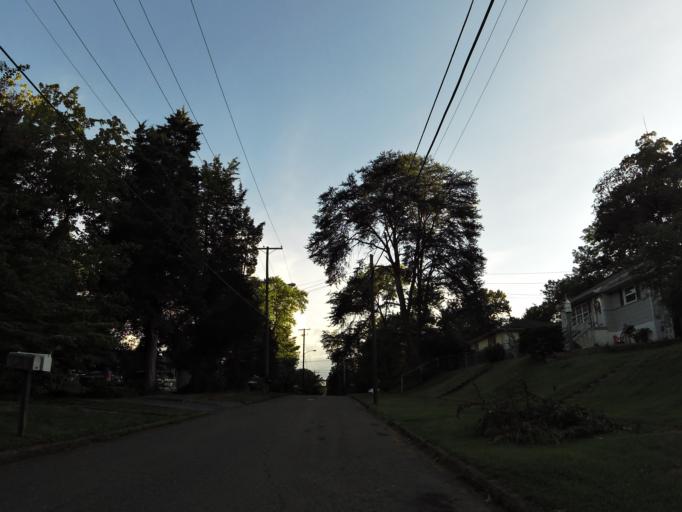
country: US
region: Tennessee
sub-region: Knox County
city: Knoxville
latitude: 36.0066
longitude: -83.9323
